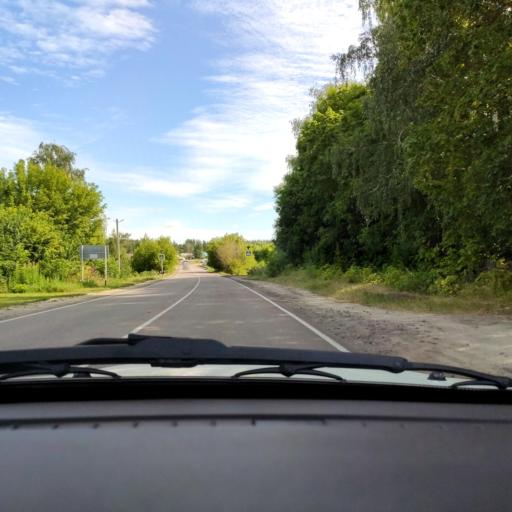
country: RU
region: Voronezj
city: Uglyanets
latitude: 51.8564
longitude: 39.6683
